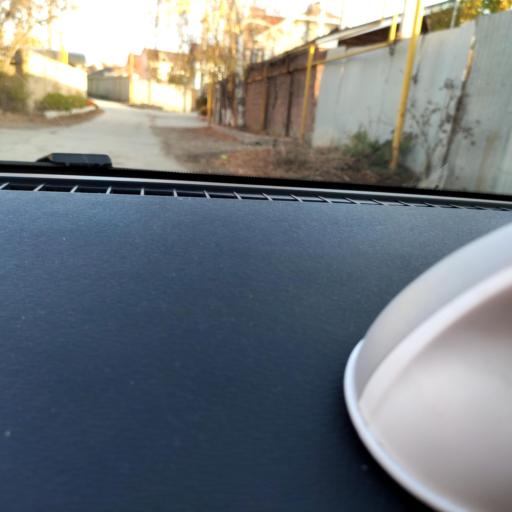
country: RU
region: Samara
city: Samara
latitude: 53.2277
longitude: 50.1589
